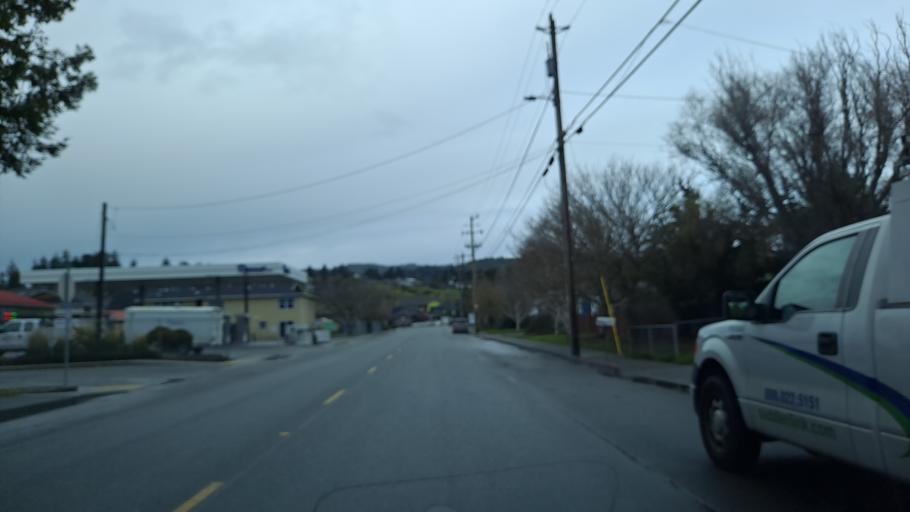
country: US
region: California
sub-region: Humboldt County
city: Fortuna
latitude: 40.5911
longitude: -124.1408
